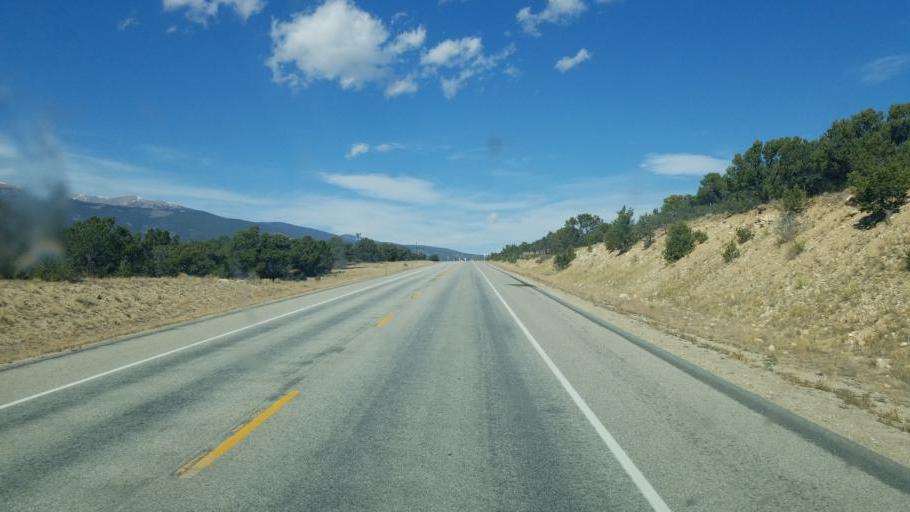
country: US
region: Colorado
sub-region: Chaffee County
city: Buena Vista
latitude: 38.8703
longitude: -106.1557
